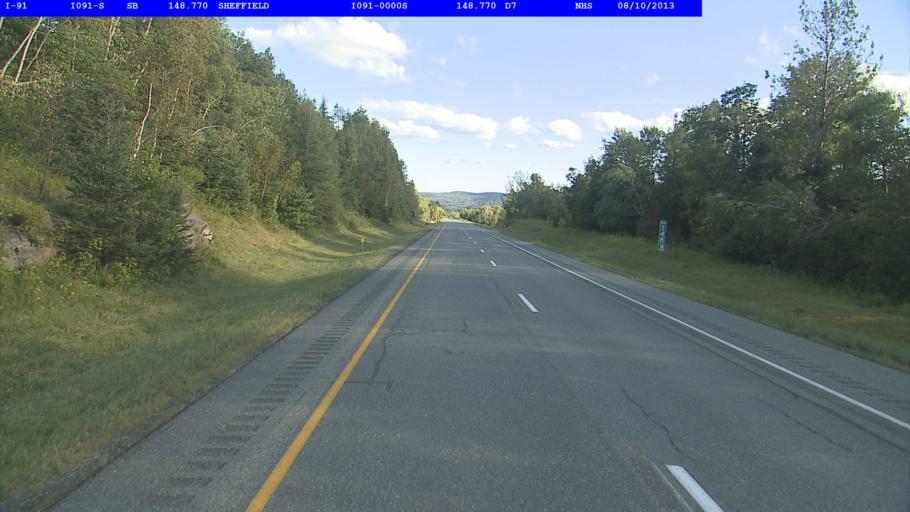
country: US
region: Vermont
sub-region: Caledonia County
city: Lyndonville
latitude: 44.6469
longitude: -72.1333
